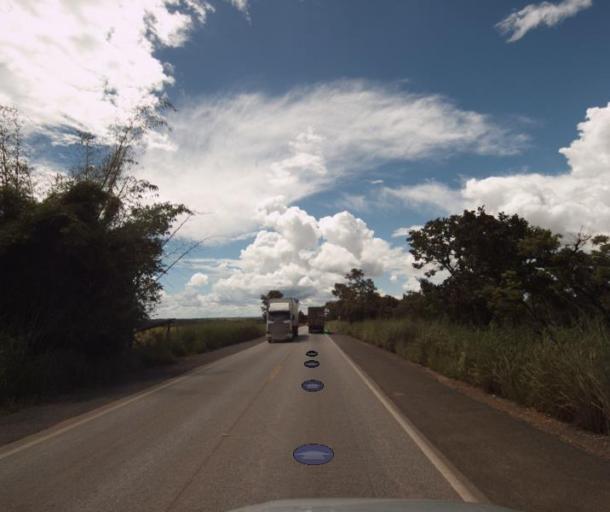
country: BR
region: Goias
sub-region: Uruacu
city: Uruacu
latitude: -14.1072
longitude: -49.1034
